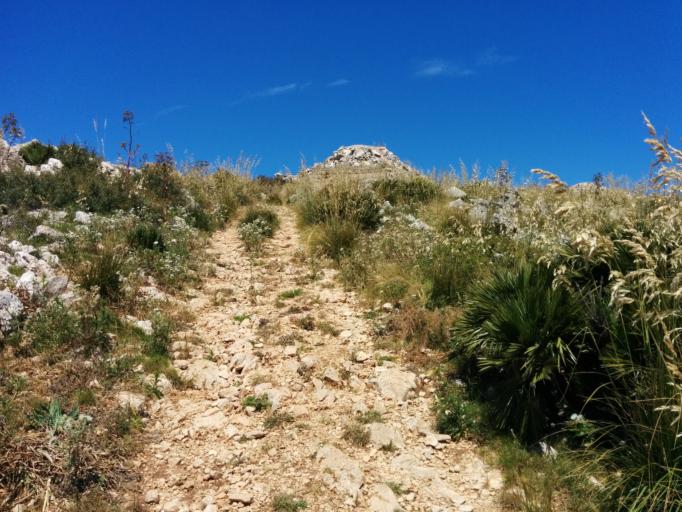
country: IT
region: Sicily
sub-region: Trapani
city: San Vito Lo Capo
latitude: 38.1655
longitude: 12.7581
